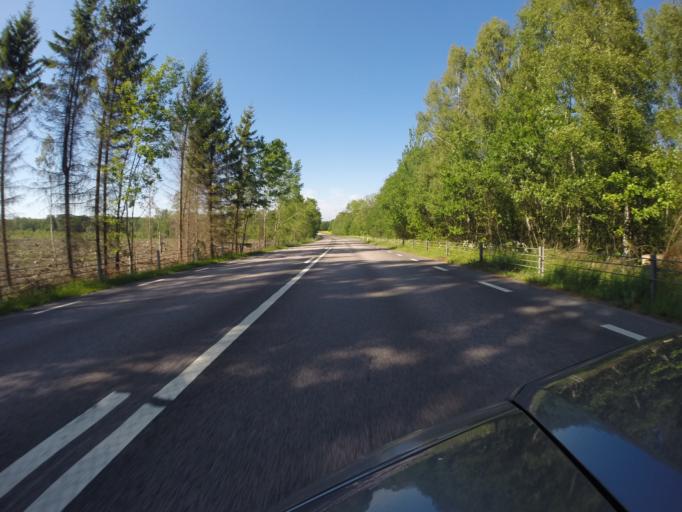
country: SE
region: Skane
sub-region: Bjuvs Kommun
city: Billesholm
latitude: 56.0377
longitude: 12.9698
